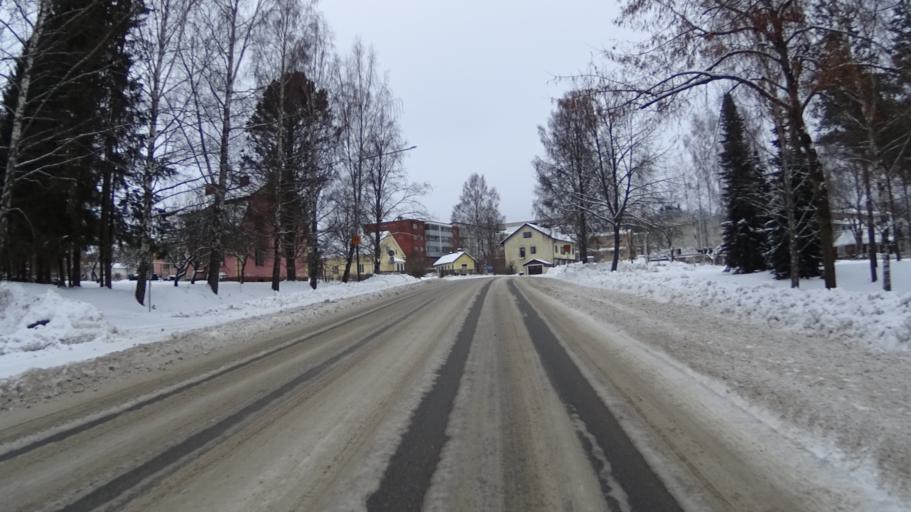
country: FI
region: Uusimaa
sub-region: Helsinki
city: Karkkila
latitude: 60.5319
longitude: 24.2081
